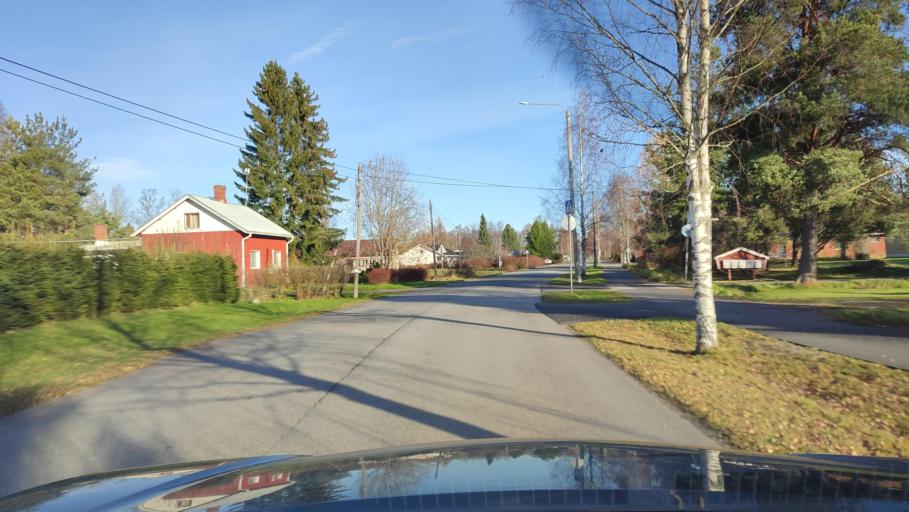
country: FI
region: Southern Ostrobothnia
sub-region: Suupohja
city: Teuva
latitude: 62.4772
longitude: 21.7466
